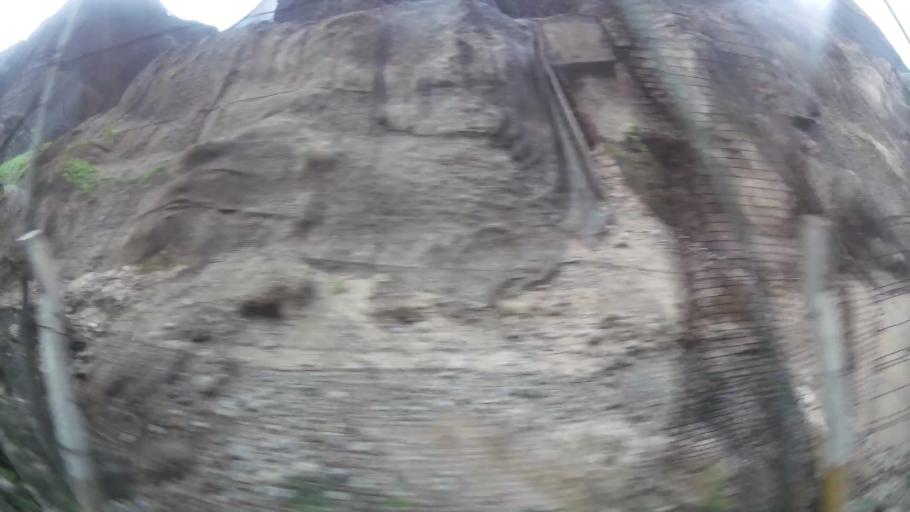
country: PE
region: Lima
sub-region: Lima
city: San Isidro
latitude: -12.1289
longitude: -77.0361
